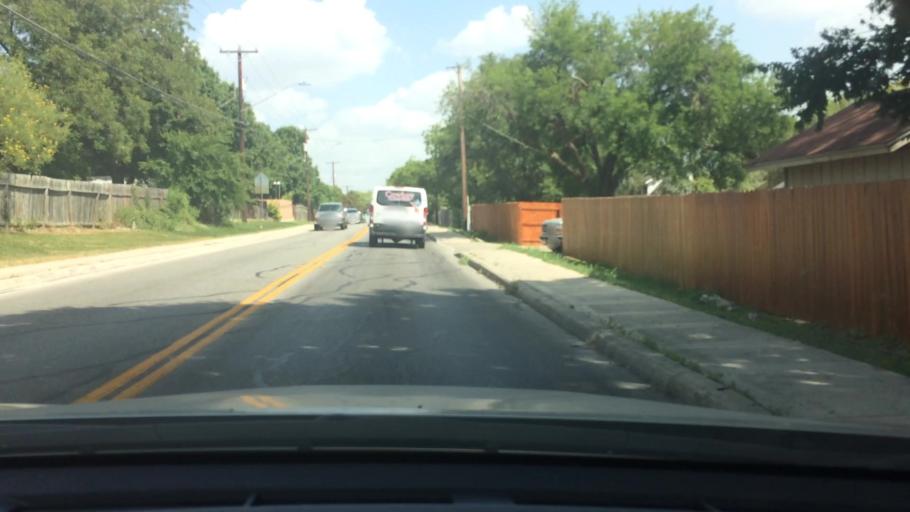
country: US
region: Texas
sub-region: Bexar County
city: Castle Hills
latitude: 29.5345
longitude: -98.5007
